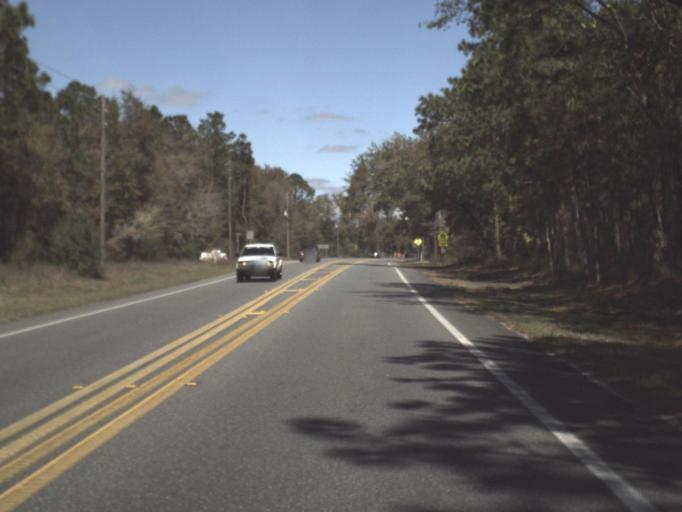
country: US
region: Florida
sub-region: Wakulla County
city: Crawfordville
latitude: 30.0760
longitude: -84.3893
